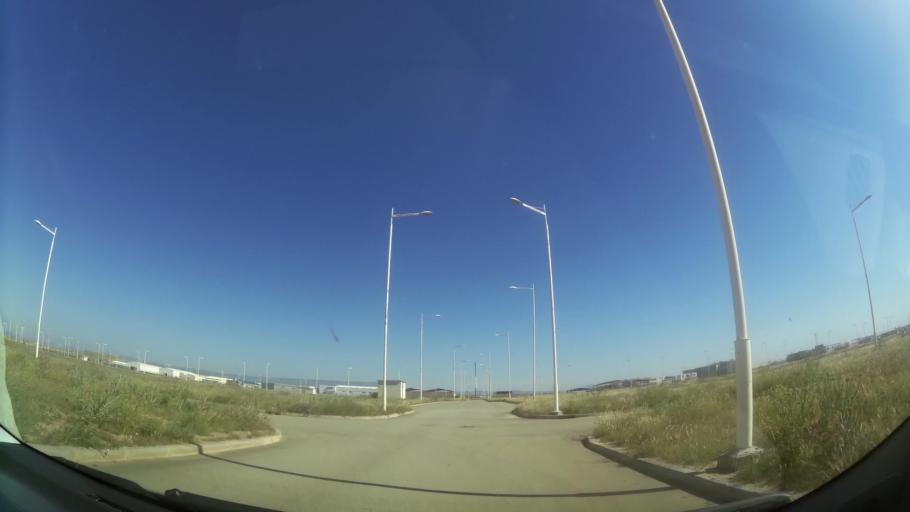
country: MA
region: Oriental
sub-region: Oujda-Angad
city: Oujda
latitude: 34.7743
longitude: -1.9358
